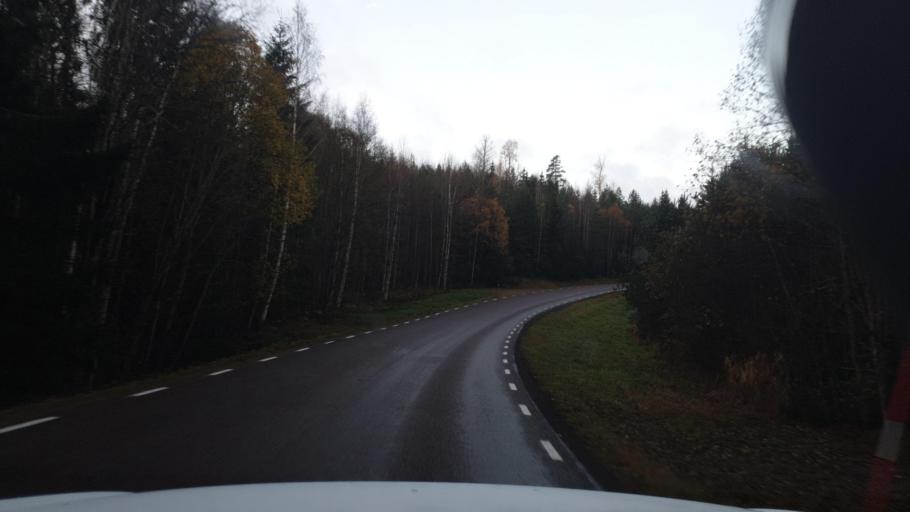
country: SE
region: Vaermland
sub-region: Arvika Kommun
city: Arvika
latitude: 59.6095
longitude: 12.7764
